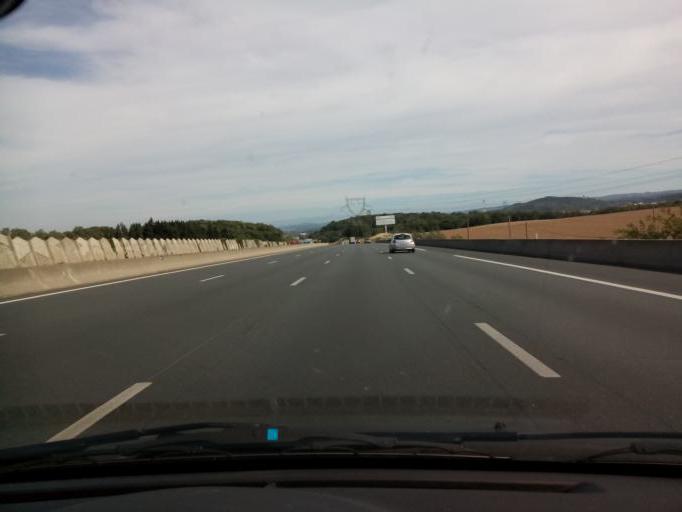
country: FR
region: Rhone-Alpes
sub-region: Departement de l'Isere
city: Grenay
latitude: 45.6577
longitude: 5.0806
